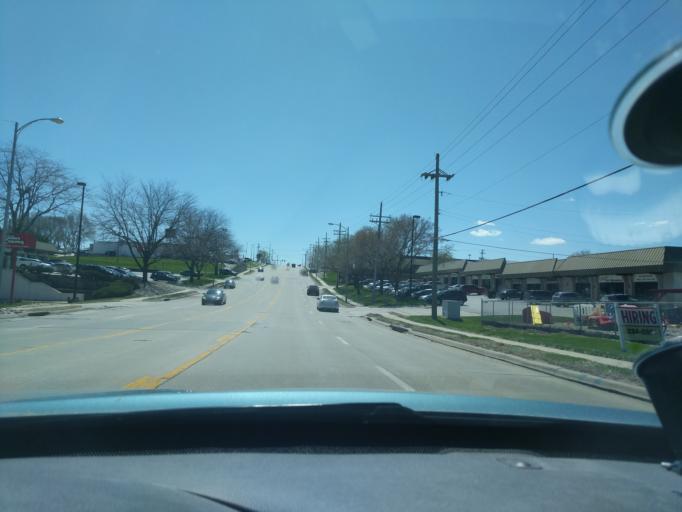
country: US
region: Nebraska
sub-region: Douglas County
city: Ralston
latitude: 41.2379
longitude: -96.1007
